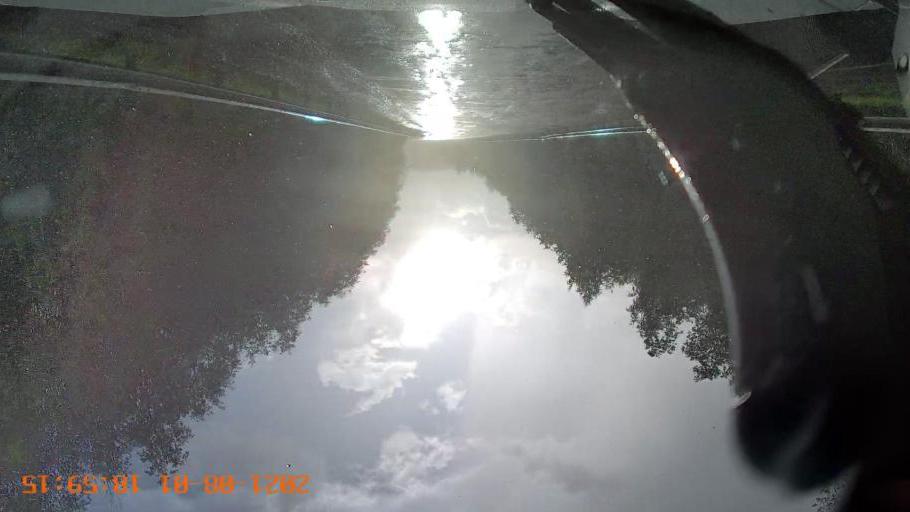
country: RU
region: Leningrad
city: Podporozh'ye
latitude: 60.9004
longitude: 34.6693
